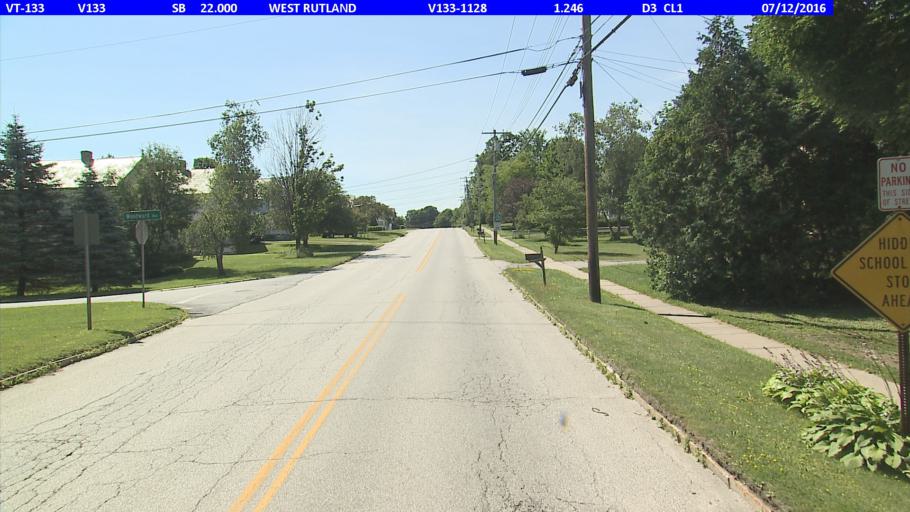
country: US
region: Vermont
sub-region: Rutland County
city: West Rutland
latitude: 43.5864
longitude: -73.0450
